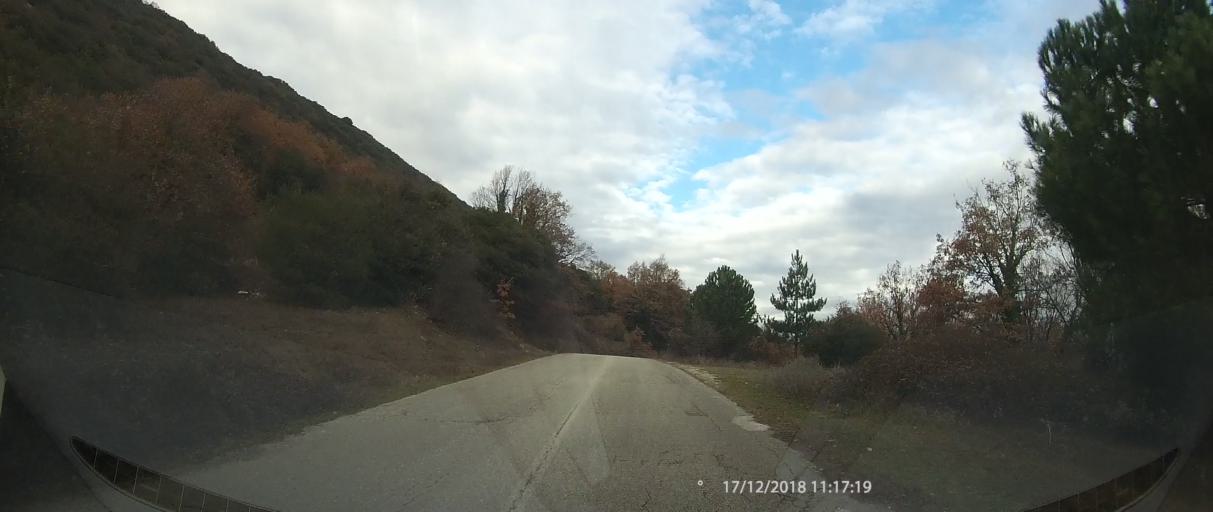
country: GR
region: Epirus
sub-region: Nomos Ioanninon
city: Kalpaki
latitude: 39.9438
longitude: 20.6635
